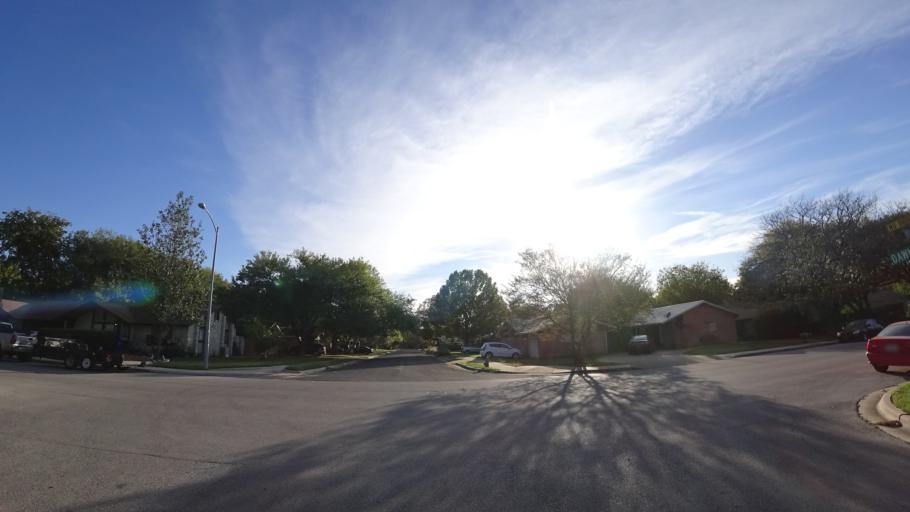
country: US
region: Texas
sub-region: Williamson County
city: Jollyville
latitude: 30.3740
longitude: -97.7337
